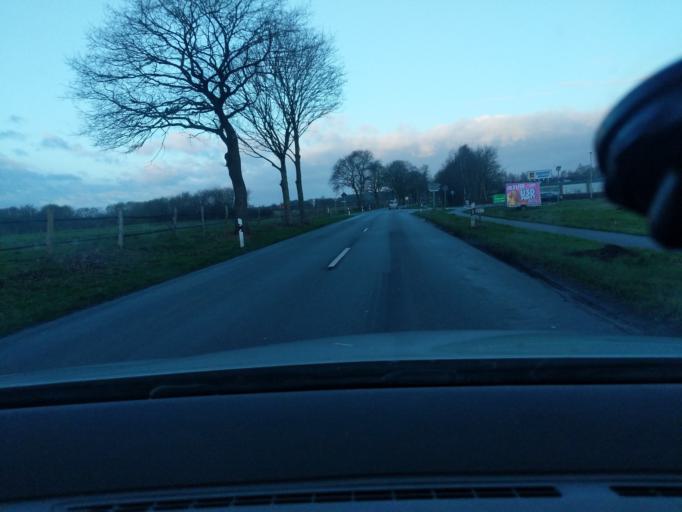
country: DE
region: Lower Saxony
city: Flogeln
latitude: 53.6264
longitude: 8.8126
